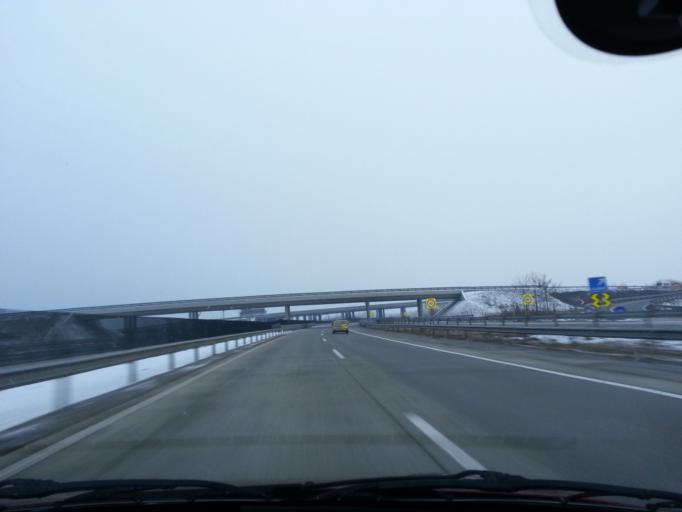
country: HU
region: Pest
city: Vecses
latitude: 47.4073
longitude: 19.3161
